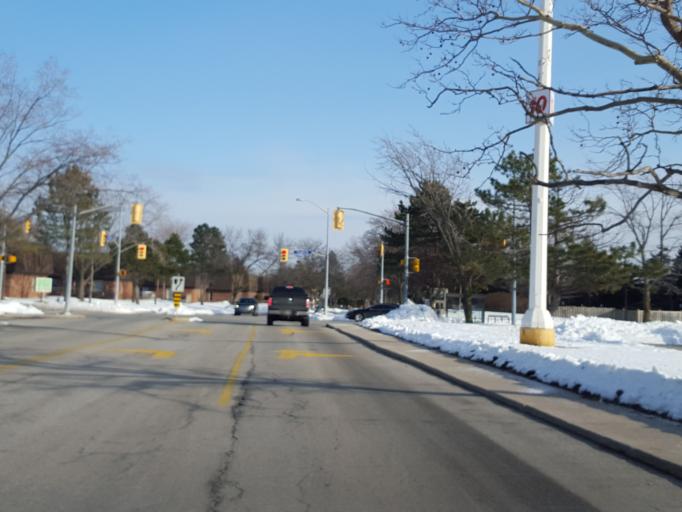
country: CA
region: Ontario
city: Burlington
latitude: 43.3496
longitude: -79.7907
